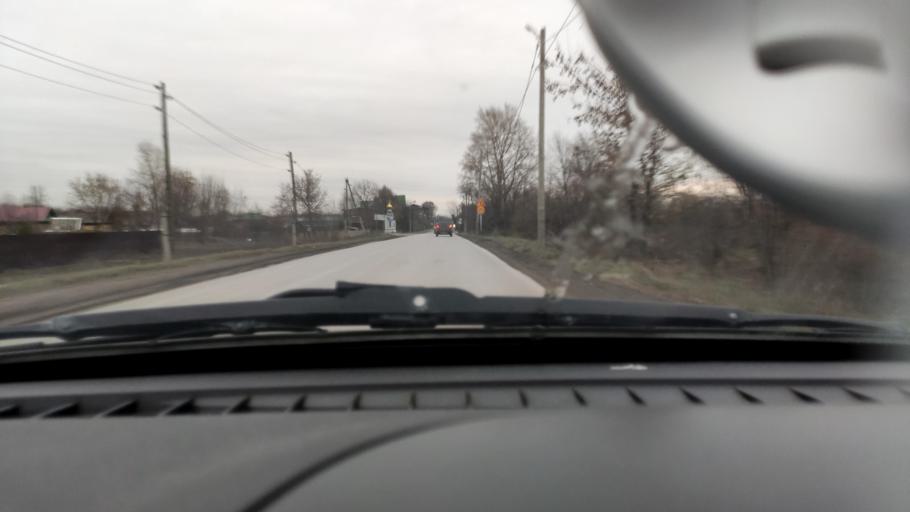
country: RU
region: Perm
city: Kondratovo
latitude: 57.9681
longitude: 56.1168
